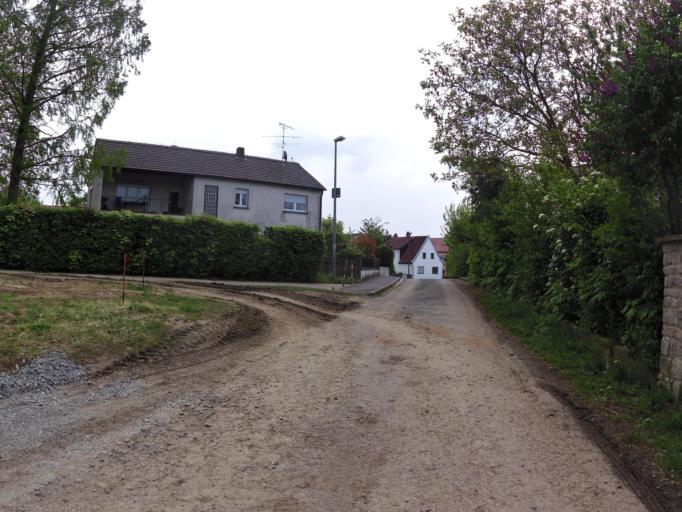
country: DE
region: Bavaria
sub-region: Regierungsbezirk Unterfranken
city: Kurnach
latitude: 49.8481
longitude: 10.0405
